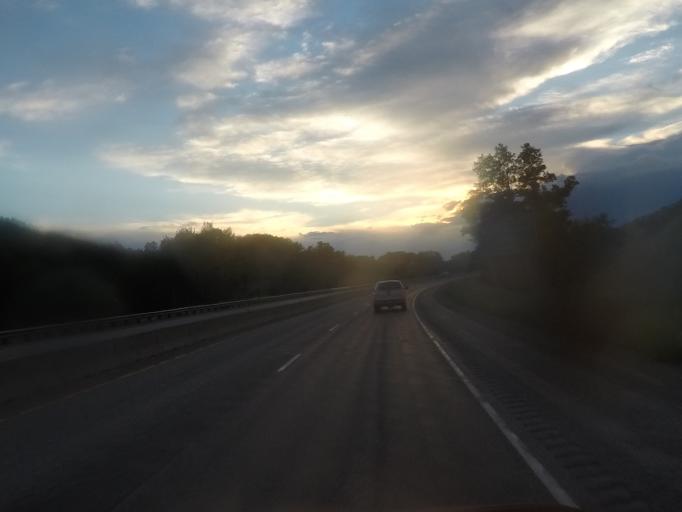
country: US
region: Montana
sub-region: Gallatin County
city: Bozeman
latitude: 45.6430
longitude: -110.9253
